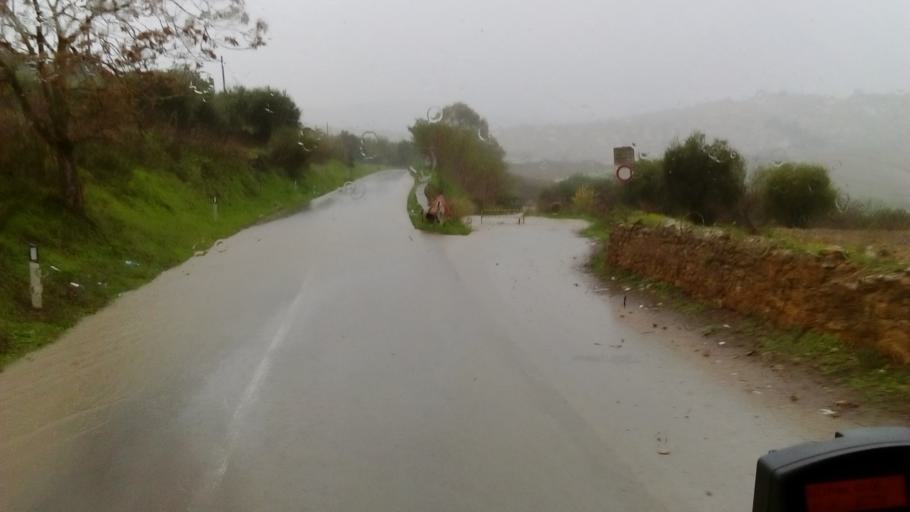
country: IT
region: Sicily
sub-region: Enna
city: Pietraperzia
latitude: 37.4193
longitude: 14.1542
